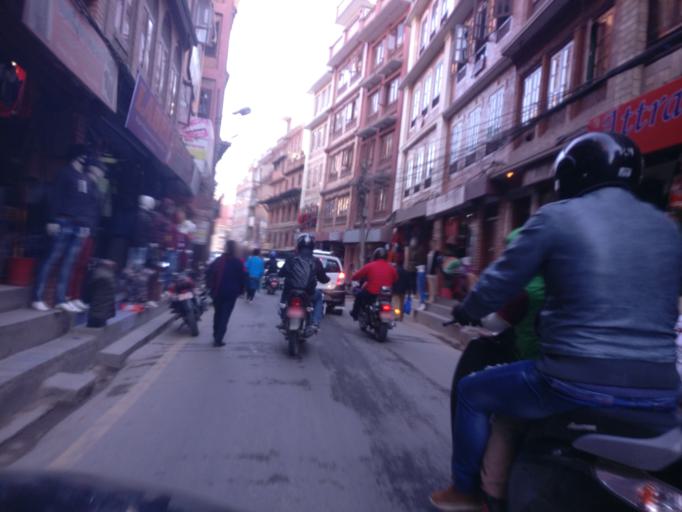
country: NP
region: Central Region
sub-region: Bagmati Zone
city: Patan
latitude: 27.6747
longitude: 85.3200
